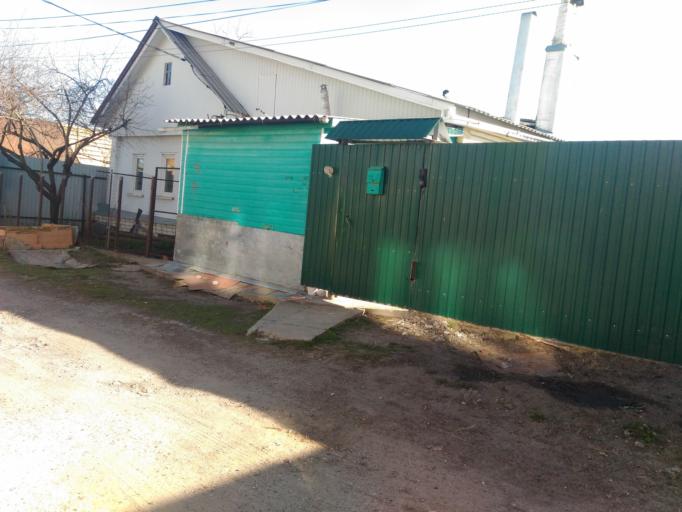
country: RU
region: Ulyanovsk
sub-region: Ulyanovskiy Rayon
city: Ulyanovsk
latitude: 54.3507
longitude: 48.3790
